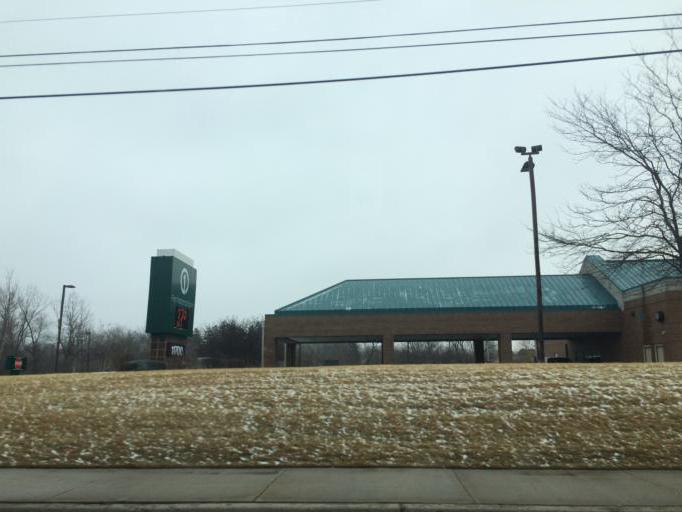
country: US
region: Illinois
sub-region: McHenry County
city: Huntley
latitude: 42.1602
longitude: -88.4290
